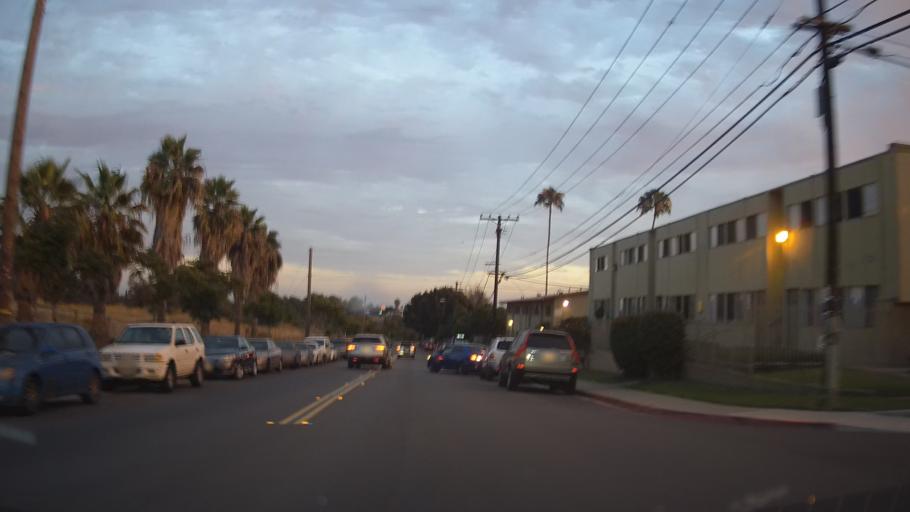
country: US
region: California
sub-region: San Diego County
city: National City
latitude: 32.7105
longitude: -117.1166
